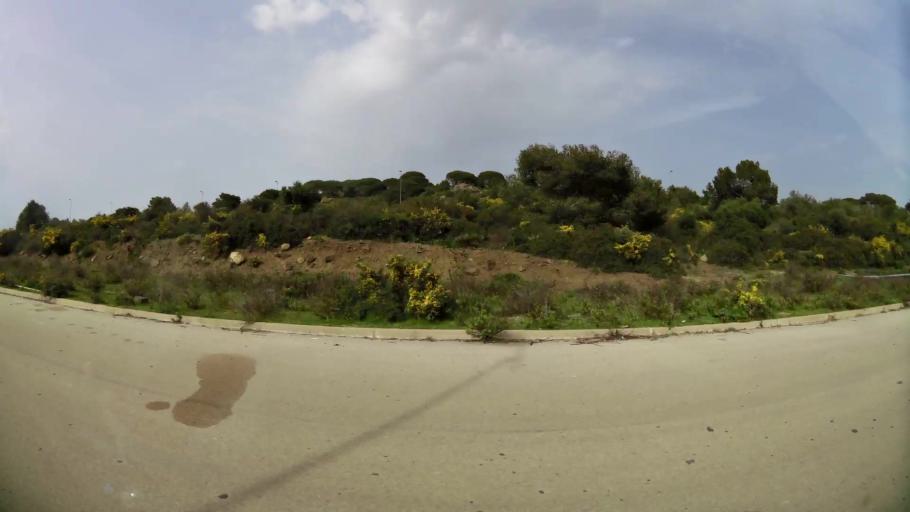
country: MA
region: Tanger-Tetouan
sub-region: Tanger-Assilah
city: Boukhalef
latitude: 35.6895
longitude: -5.9377
